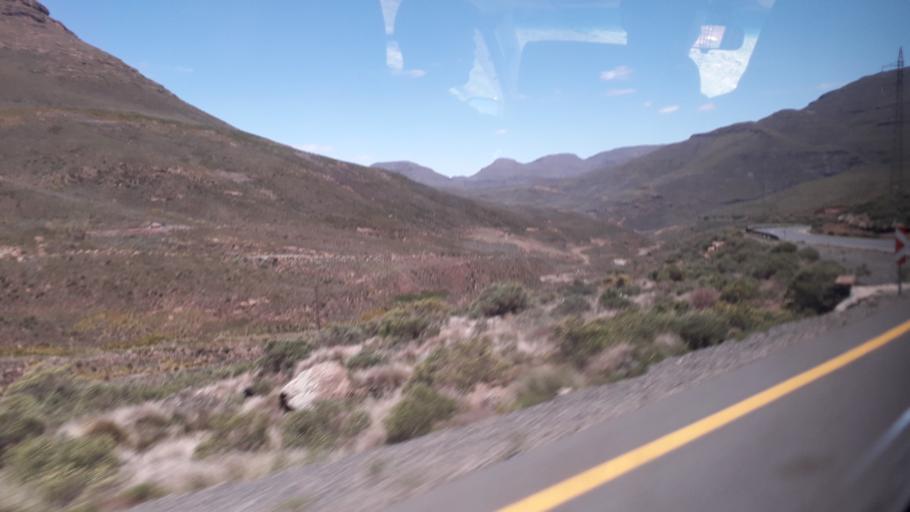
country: ZA
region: Orange Free State
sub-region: Thabo Mofutsanyana District Municipality
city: Phuthaditjhaba
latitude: -28.7714
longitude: 28.6672
